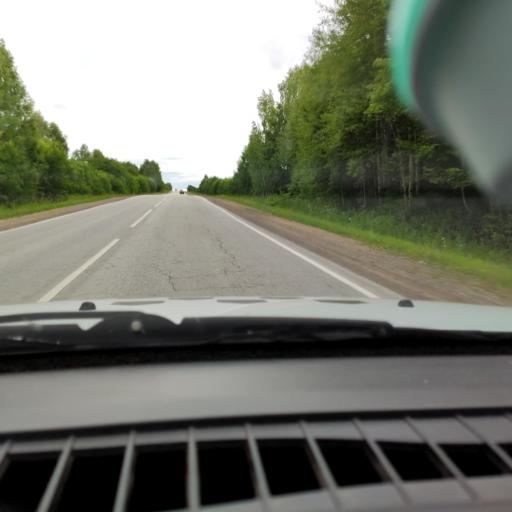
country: RU
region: Perm
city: Lys'va
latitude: 58.1398
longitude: 57.7431
